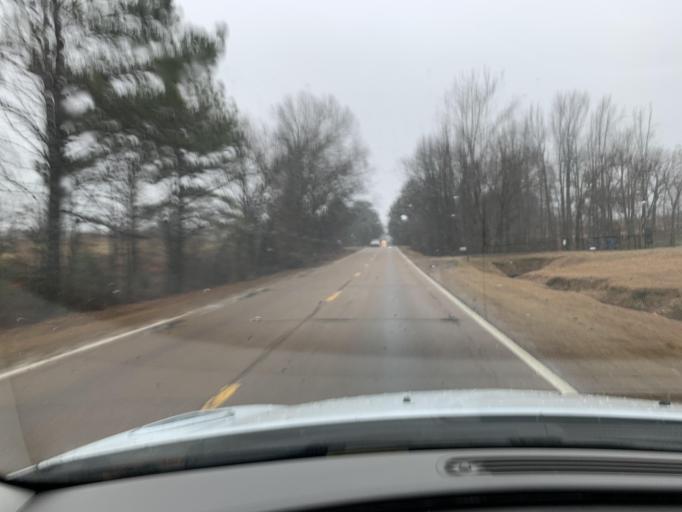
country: US
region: Mississippi
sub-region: De Soto County
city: Hernando
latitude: 34.8911
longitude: -89.9966
